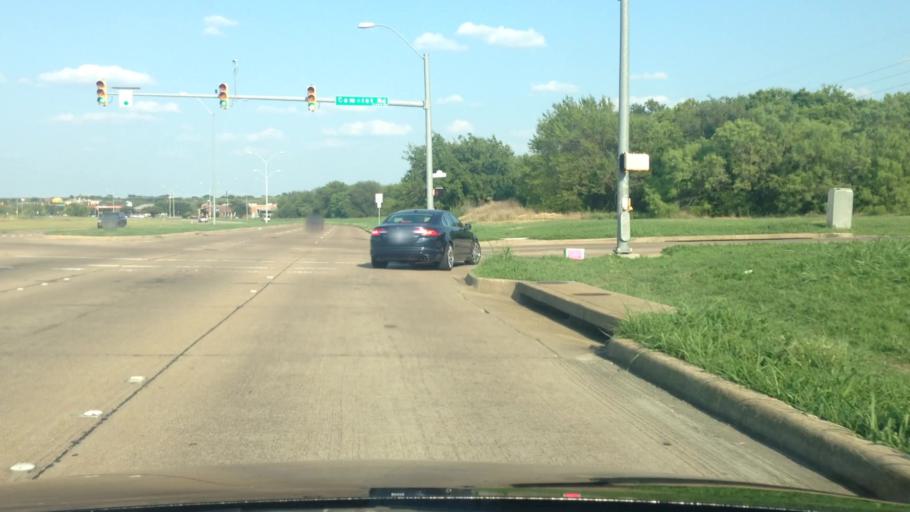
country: US
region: Texas
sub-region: Tarrant County
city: Edgecliff Village
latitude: 32.6480
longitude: -97.3407
